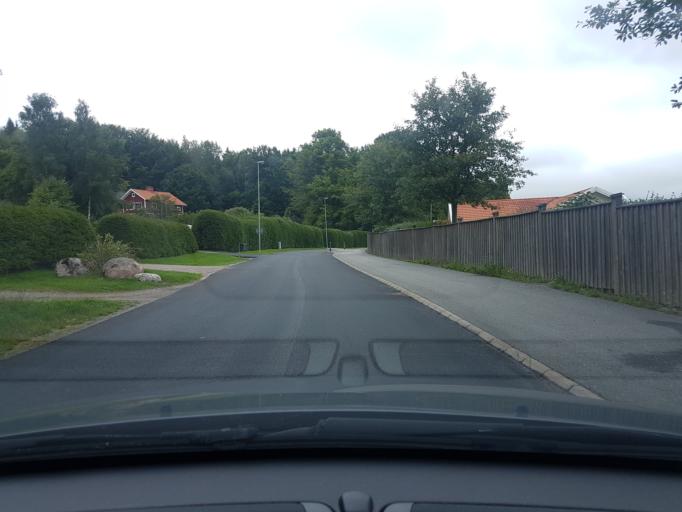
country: SE
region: Vaestra Goetaland
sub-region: Ale Kommun
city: Nodinge-Nol
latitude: 57.8859
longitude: 12.0474
